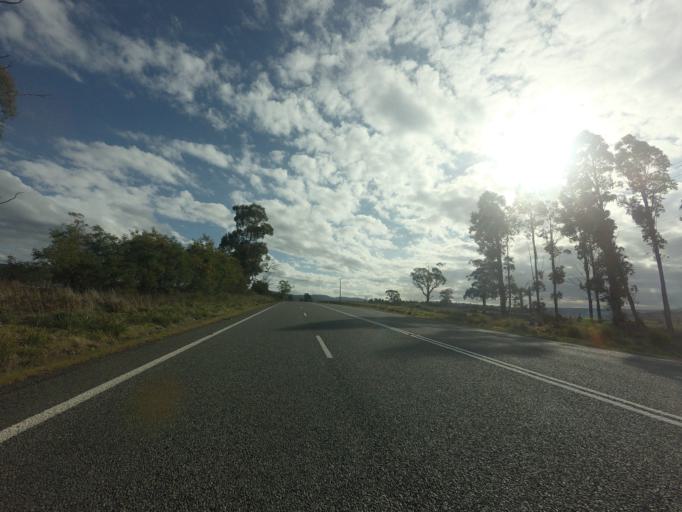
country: AU
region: Tasmania
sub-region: Sorell
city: Sorell
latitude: -42.6016
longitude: 147.7562
